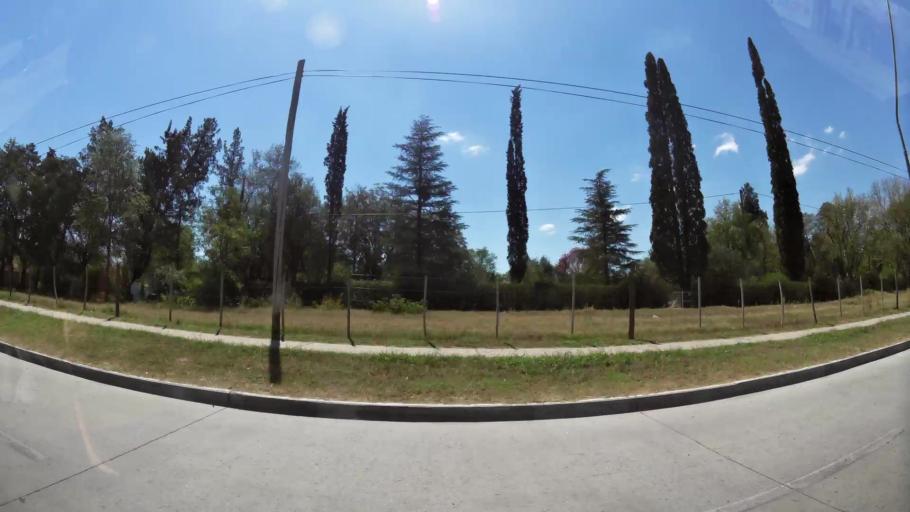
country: AR
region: Cordoba
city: Villa Allende
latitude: -31.3345
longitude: -64.2704
